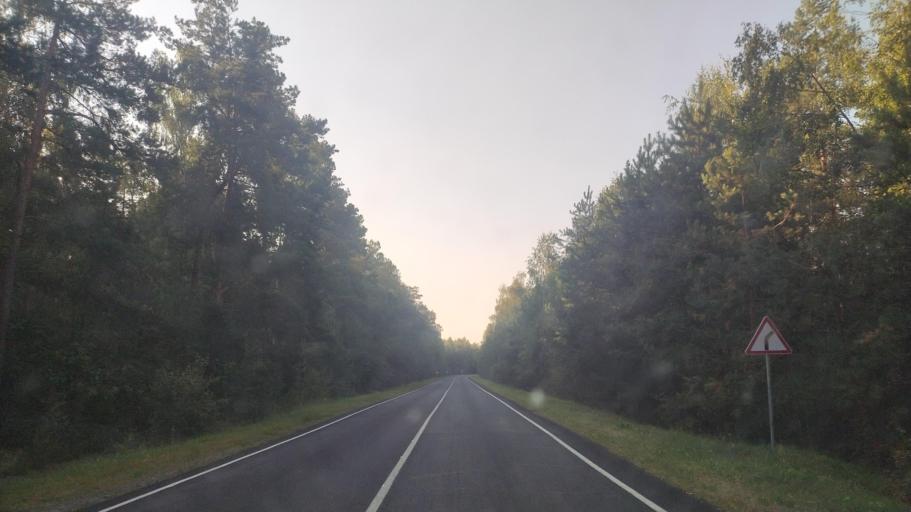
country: BY
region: Brest
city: Drahichyn
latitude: 52.2800
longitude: 25.0709
